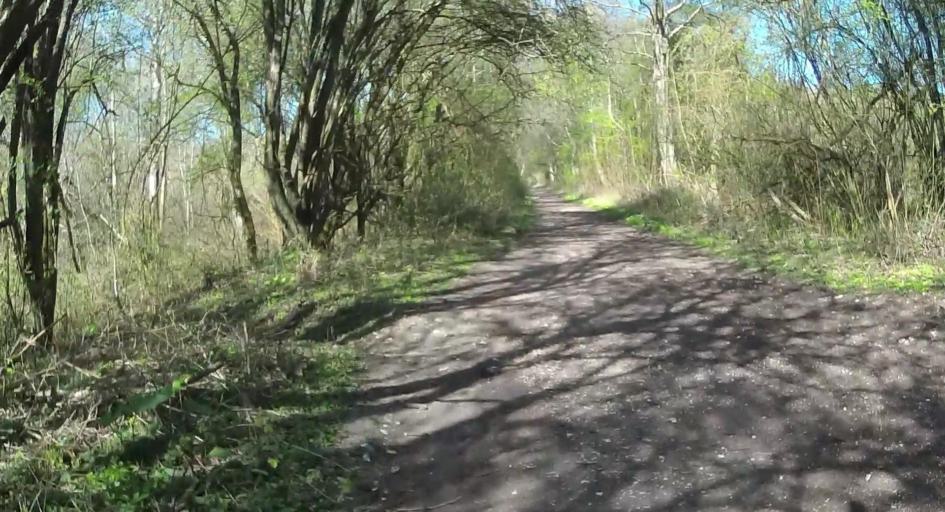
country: GB
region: England
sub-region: Hampshire
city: Romsey
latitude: 51.0884
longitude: -1.5007
